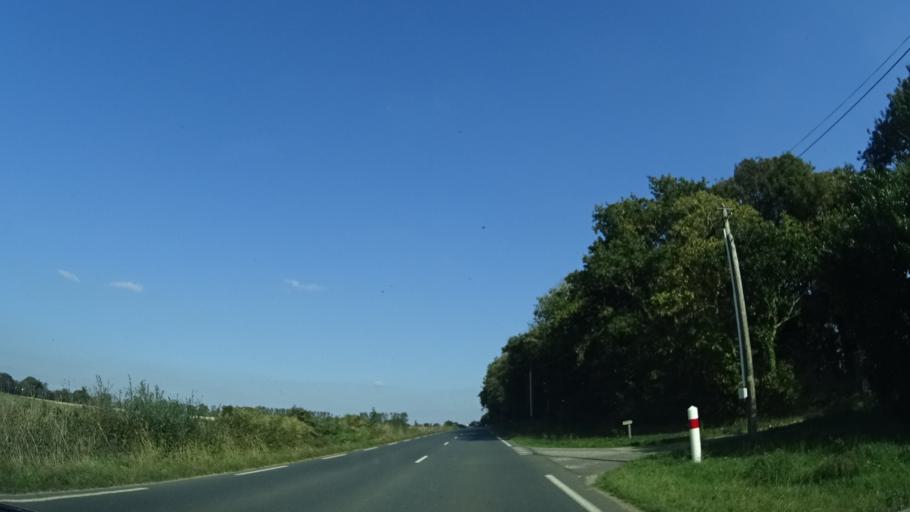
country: FR
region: Brittany
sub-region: Departement du Finistere
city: Plonevez-Porzay
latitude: 48.1301
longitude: -4.2006
